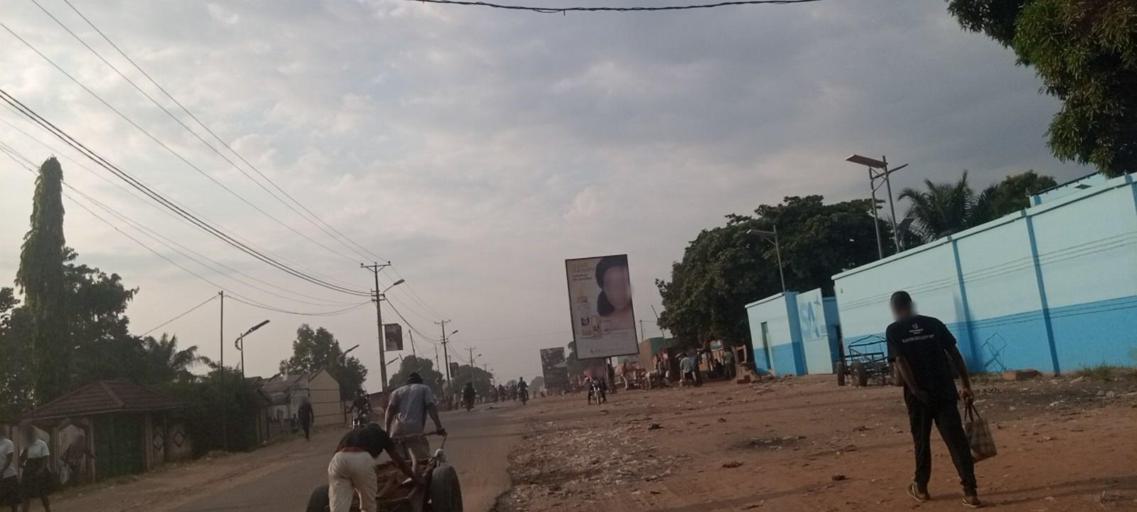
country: CD
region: Kasai-Oriental
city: Mbuji-Mayi
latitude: -6.1307
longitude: 23.6052
